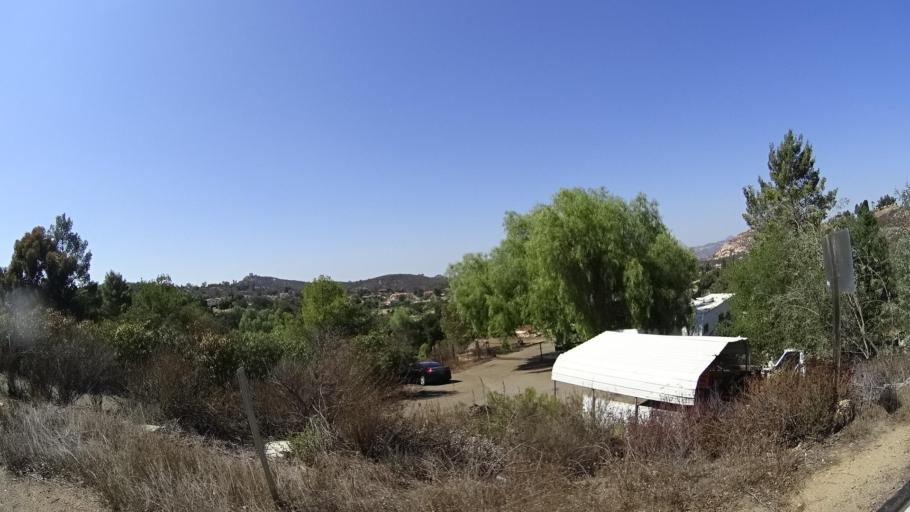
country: US
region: California
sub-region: San Diego County
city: Harbison Canyon
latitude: 32.8236
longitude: -116.8497
